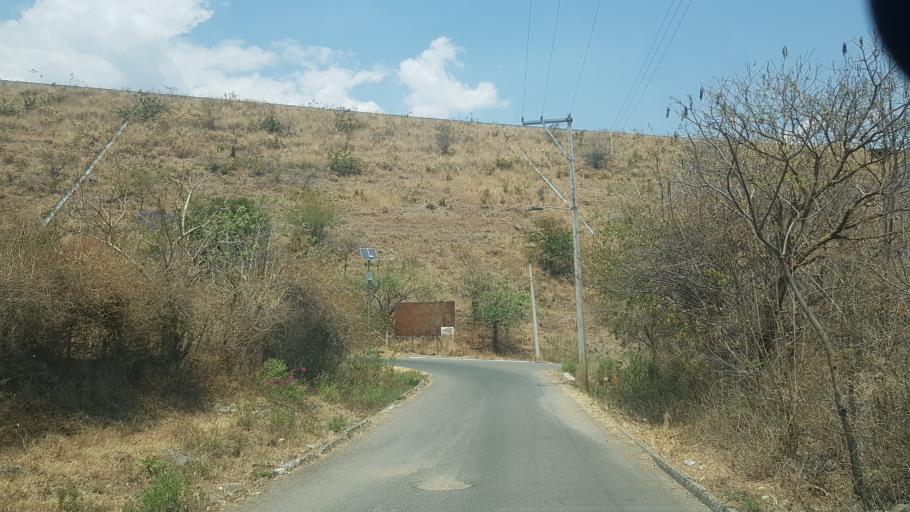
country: MX
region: Puebla
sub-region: Atzitzihuacan
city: Santiago Atzitzihuacan
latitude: 18.8293
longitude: -98.5811
